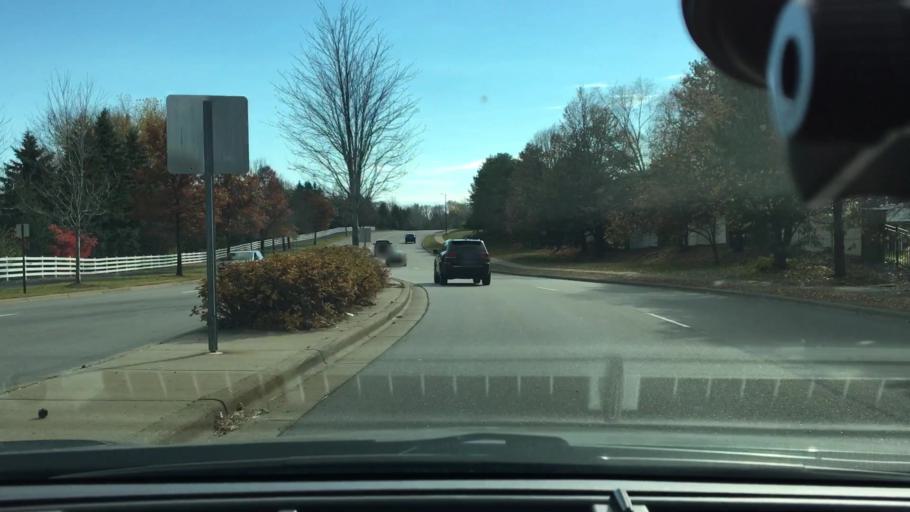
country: US
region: Minnesota
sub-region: Hennepin County
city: Maple Grove
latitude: 45.1159
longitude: -93.4925
